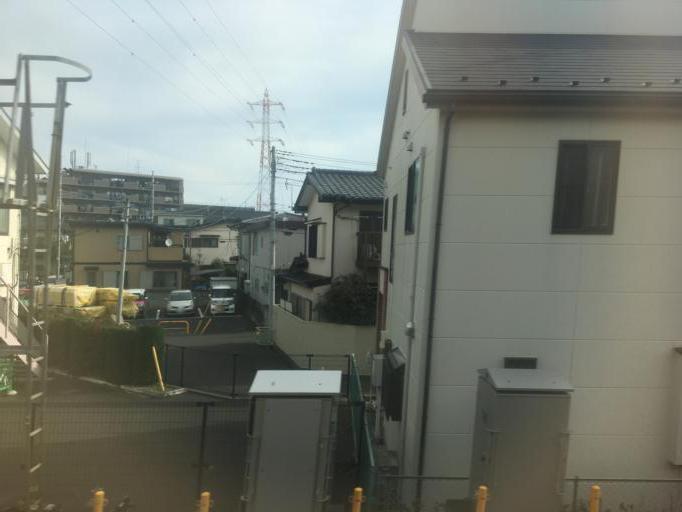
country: JP
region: Saitama
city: Sayama
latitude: 35.8176
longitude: 139.4135
